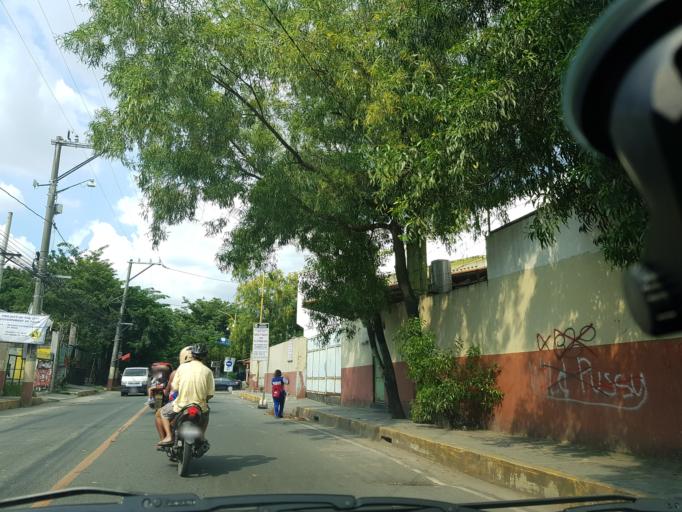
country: PH
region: Metro Manila
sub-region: Pasig
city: Pasig City
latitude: 14.5714
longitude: 121.0876
